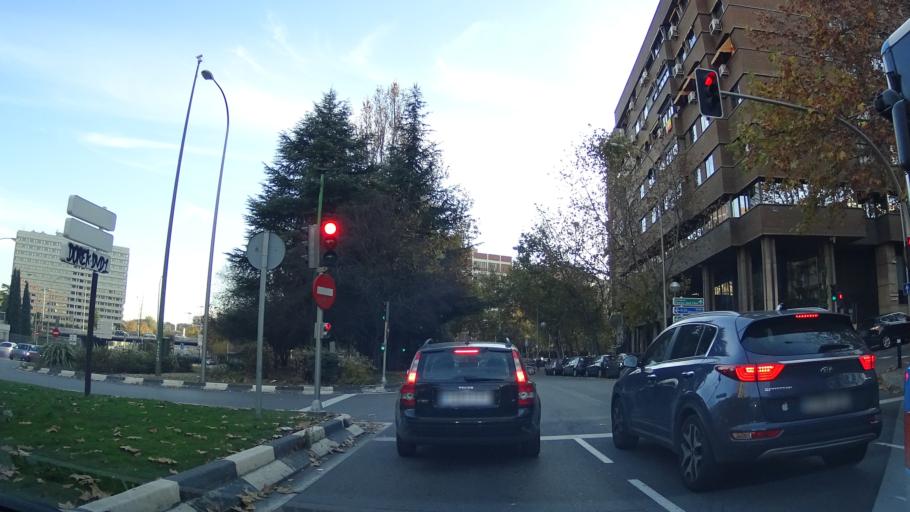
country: ES
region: Madrid
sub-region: Provincia de Madrid
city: Salamanca
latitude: 40.4437
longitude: -3.6674
